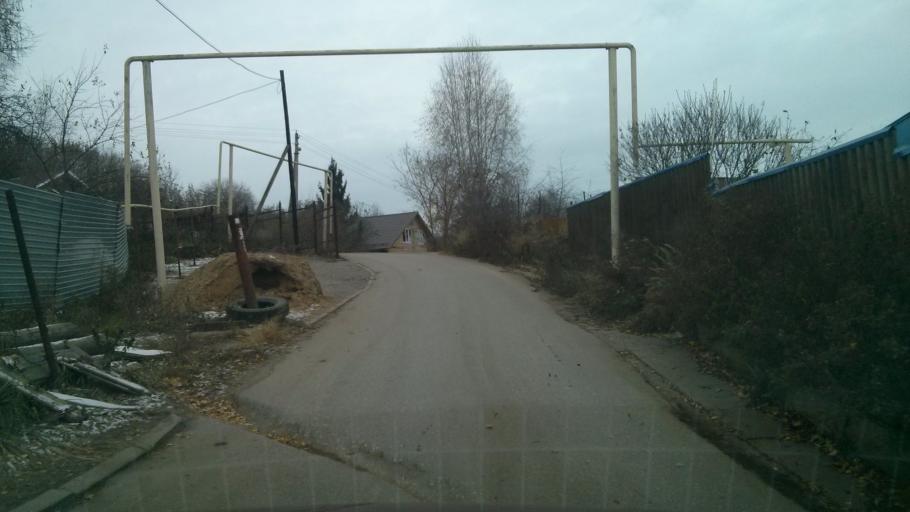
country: RU
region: Nizjnij Novgorod
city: Afonino
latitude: 56.2886
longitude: 44.0981
